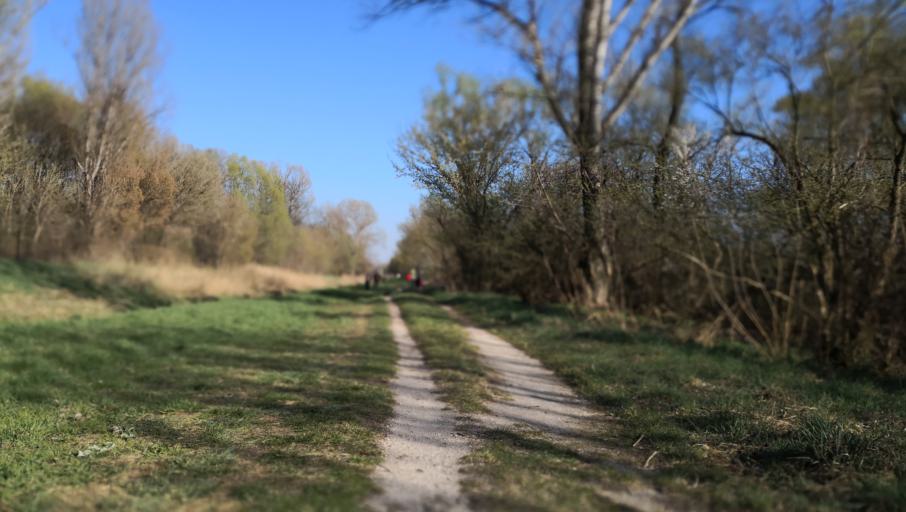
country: HU
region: Budapest
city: Budapest XVII. keruelet
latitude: 47.4863
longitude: 19.2383
